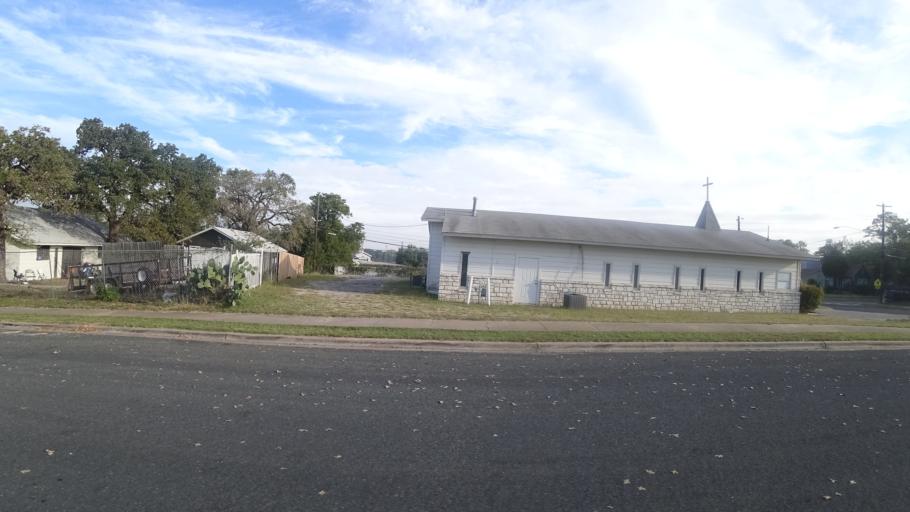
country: US
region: Texas
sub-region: Travis County
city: Austin
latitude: 30.2729
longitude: -97.7097
